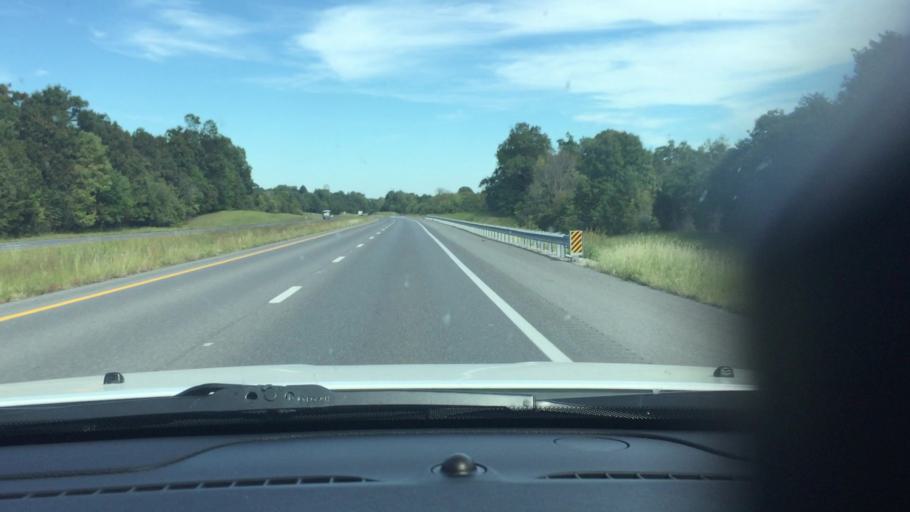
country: US
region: Kentucky
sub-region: Caldwell County
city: Princeton
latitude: 37.1145
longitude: -87.9296
